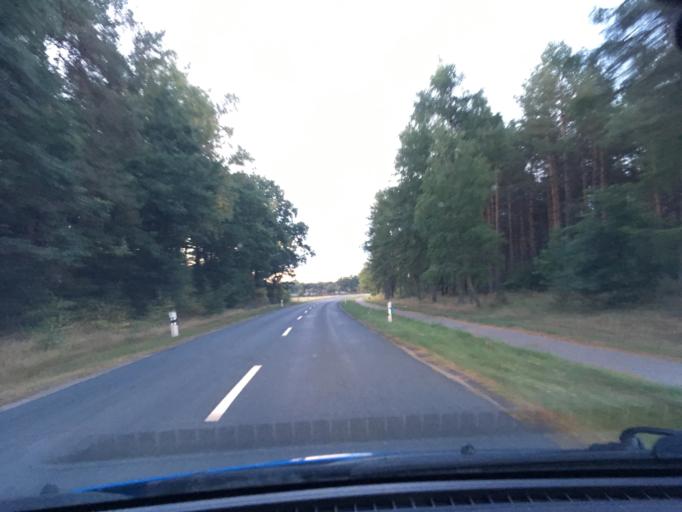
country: DE
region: Lower Saxony
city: Fassberg
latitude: 52.9188
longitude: 10.1501
